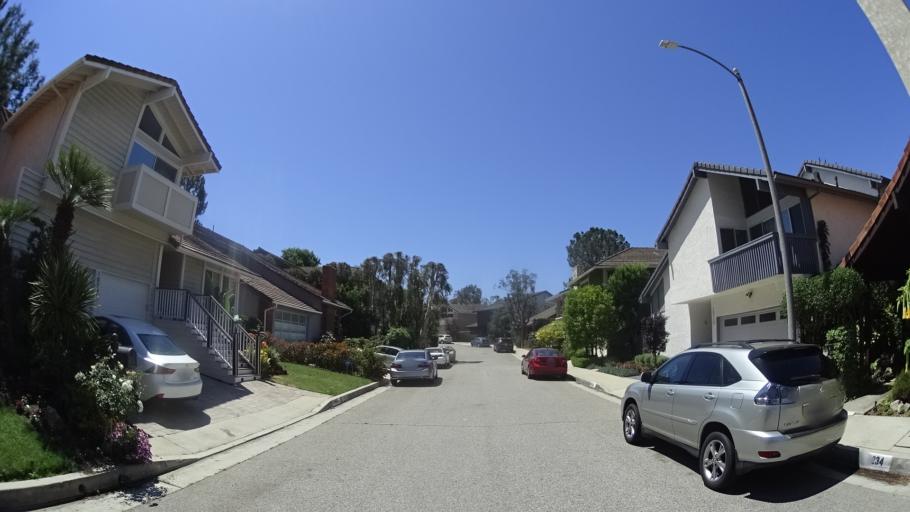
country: US
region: California
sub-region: Los Angeles County
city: Sherman Oaks
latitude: 34.1259
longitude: -118.4438
